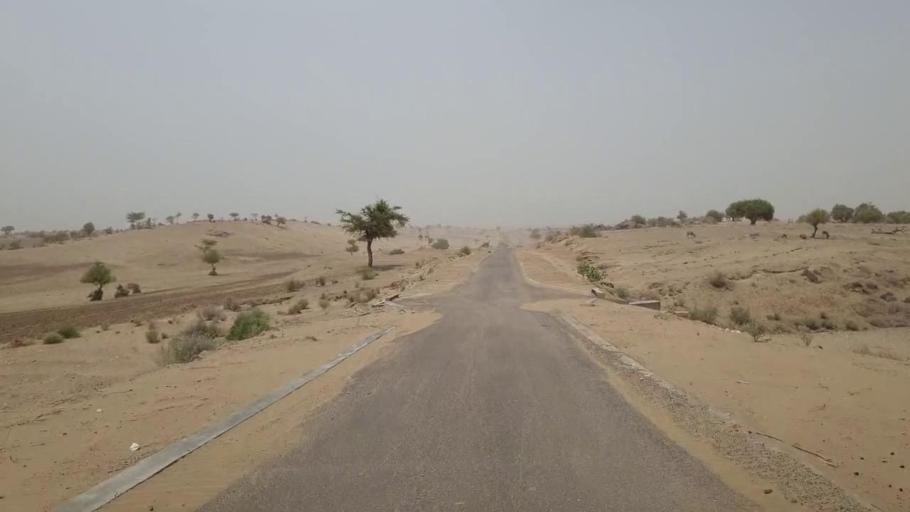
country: PK
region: Sindh
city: Islamkot
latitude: 24.8017
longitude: 70.5220
